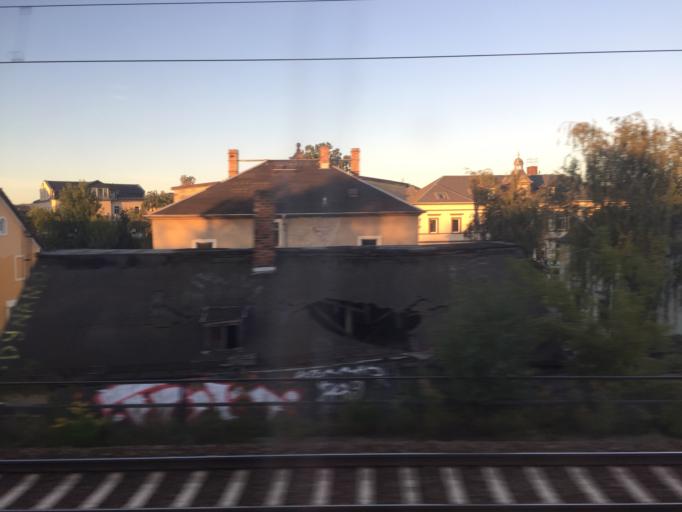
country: DE
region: Saxony
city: Heidenau
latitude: 50.9730
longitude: 13.8727
